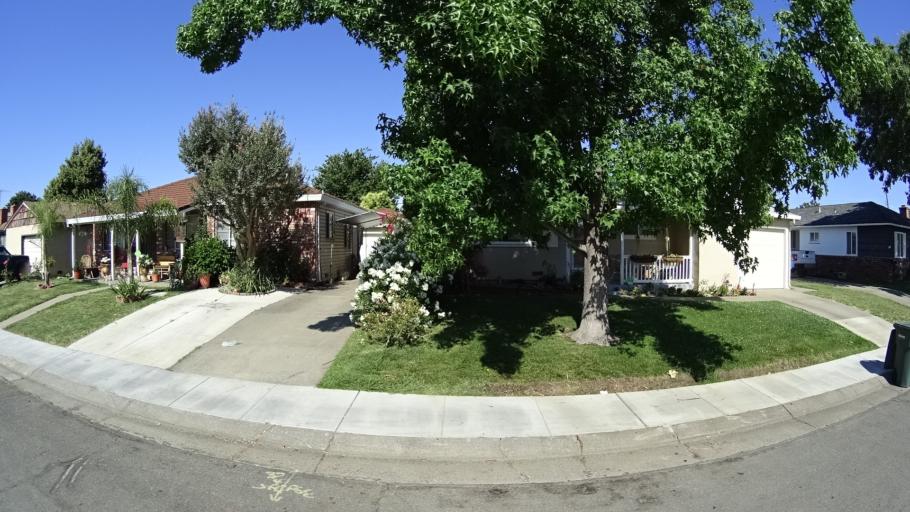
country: US
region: California
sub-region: Sacramento County
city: Florin
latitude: 38.5287
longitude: -121.4210
